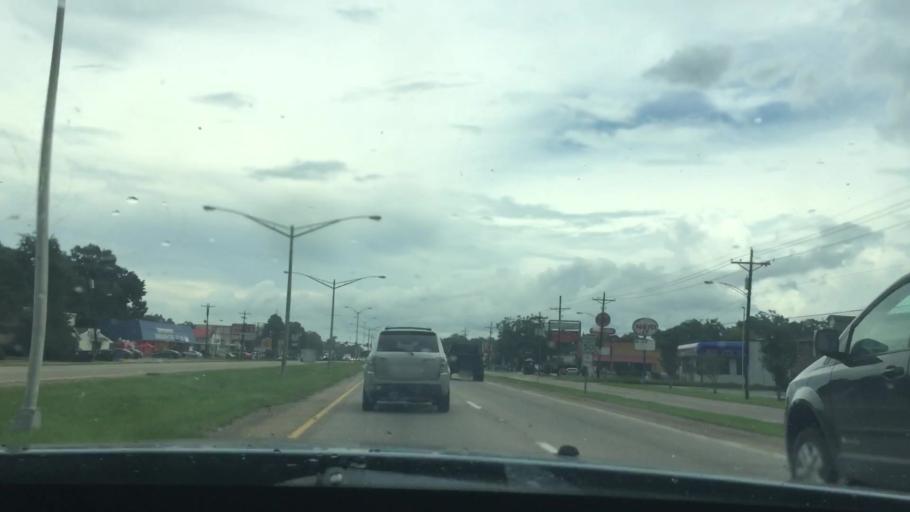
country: US
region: Louisiana
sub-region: East Baton Rouge Parish
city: Monticello
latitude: 30.4570
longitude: -91.0695
